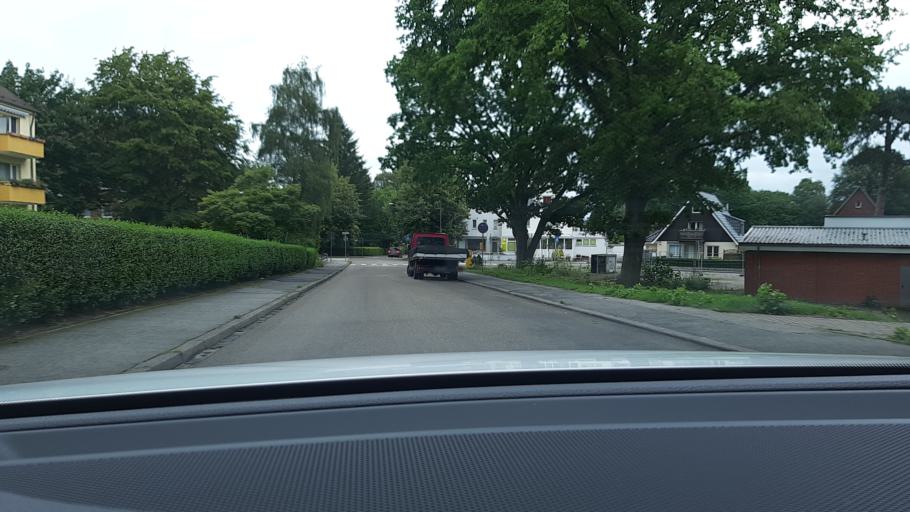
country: DE
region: Schleswig-Holstein
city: Luebeck
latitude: 53.8892
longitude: 10.7104
